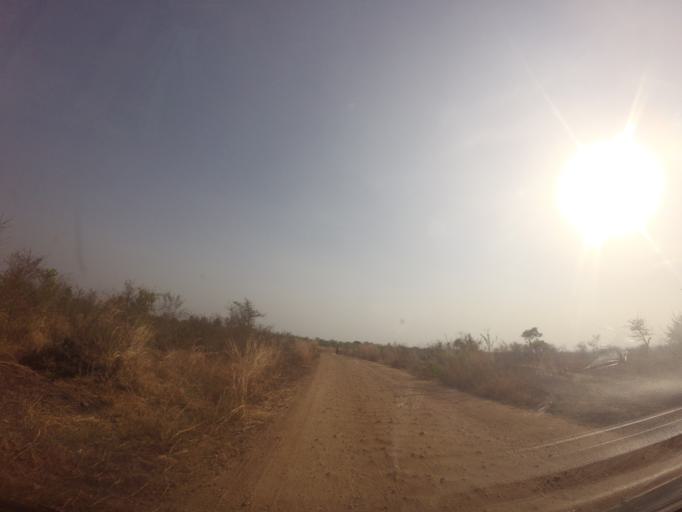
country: UG
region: Northern Region
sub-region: Maracha District
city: Maracha
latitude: 3.1170
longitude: 31.1568
